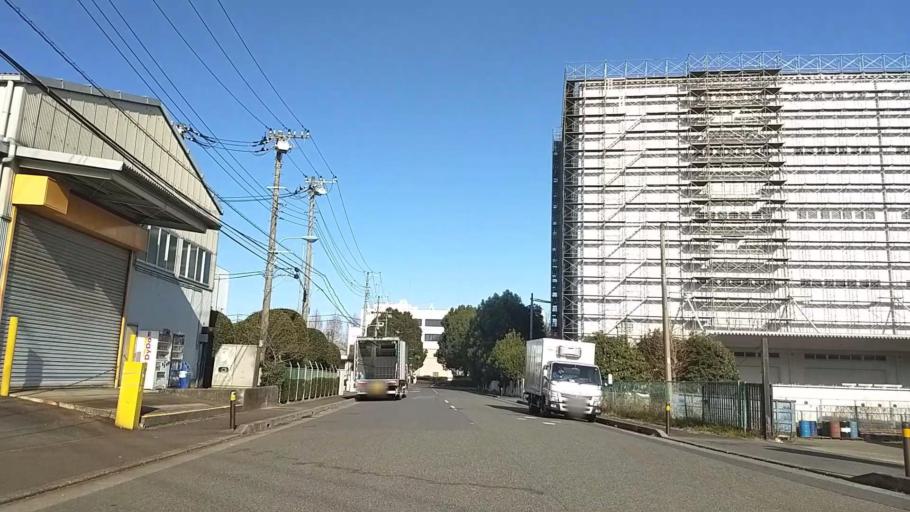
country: JP
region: Kanagawa
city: Atsugi
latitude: 35.4595
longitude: 139.3249
